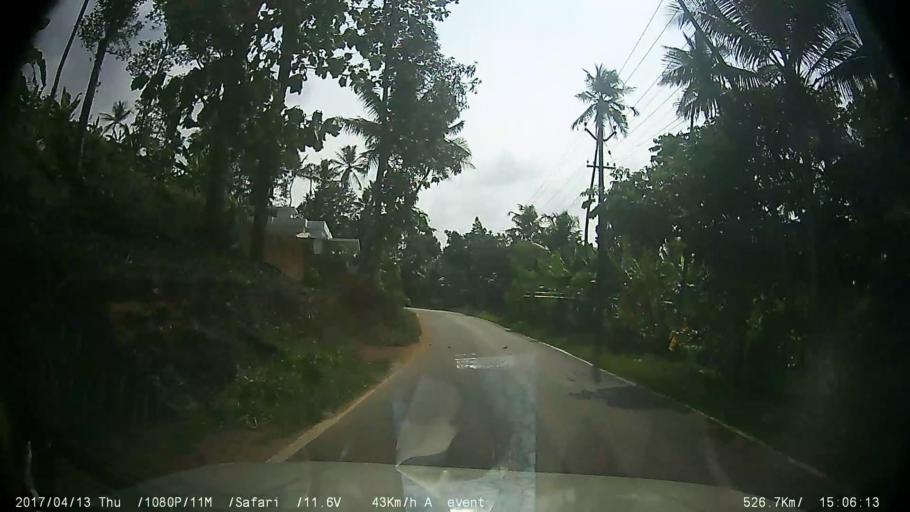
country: IN
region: Kerala
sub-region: Ernakulam
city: Ramamangalam
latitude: 9.9191
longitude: 76.4810
